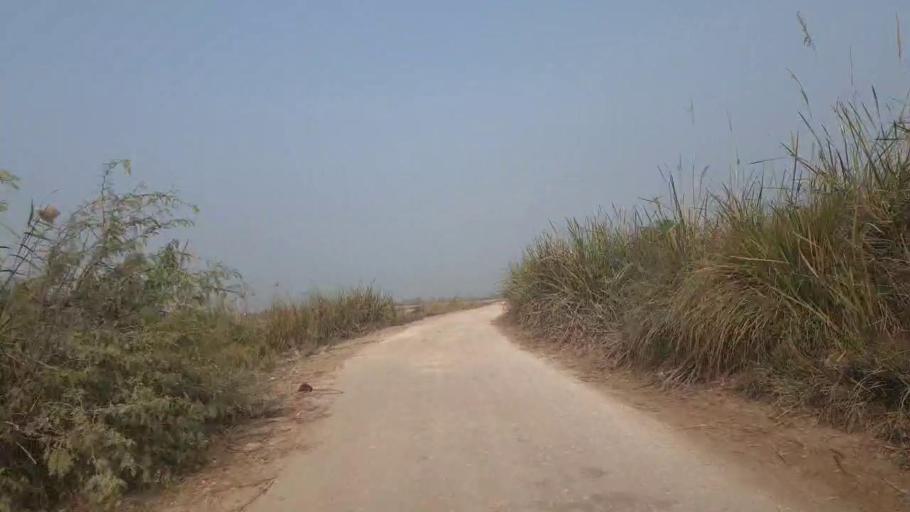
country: PK
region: Sindh
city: Shahdadpur
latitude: 25.8944
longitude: 68.5908
